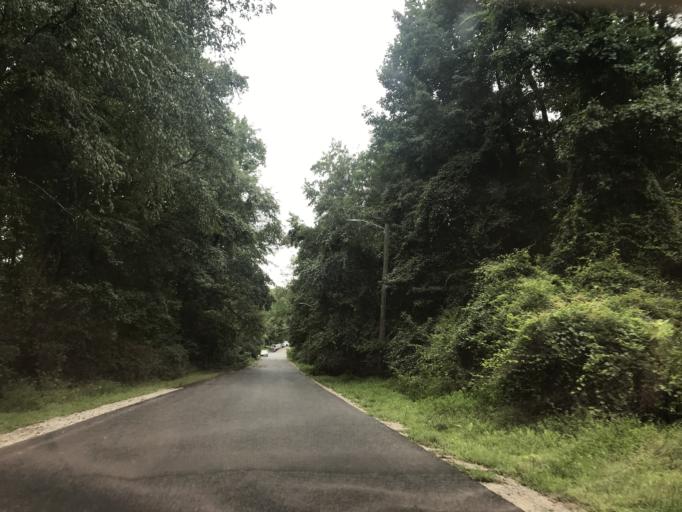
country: US
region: North Carolina
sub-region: Wake County
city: Knightdale
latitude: 35.7987
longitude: -78.5441
